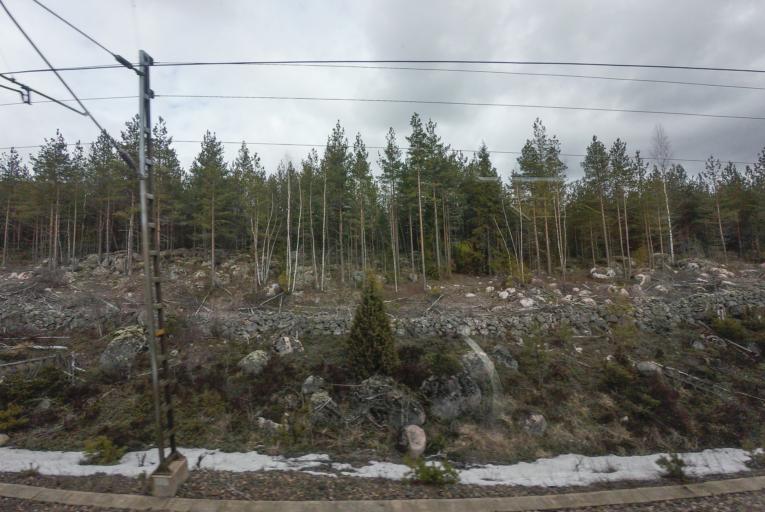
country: FI
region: Paijanne Tavastia
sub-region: Lahti
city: Artjaervi
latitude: 60.9233
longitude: 26.1405
